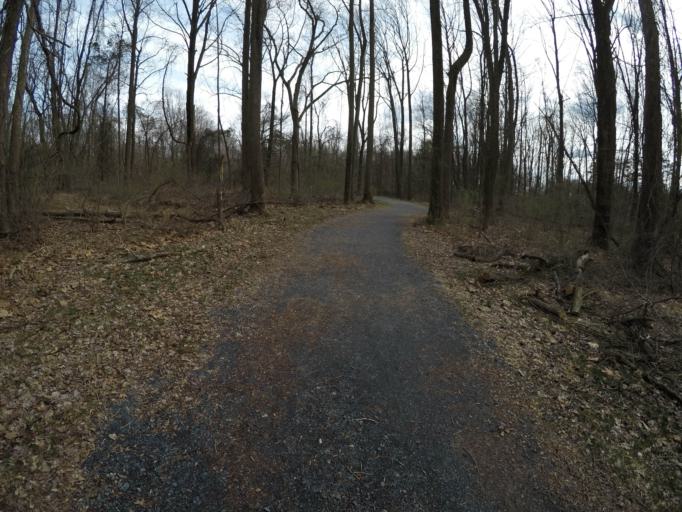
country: US
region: Maryland
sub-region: Harford County
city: Bel Air South
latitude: 39.4894
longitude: -76.3240
